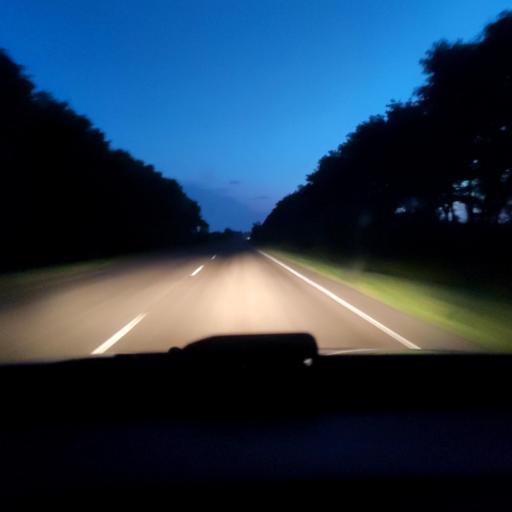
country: RU
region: Voronezj
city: Panino
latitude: 51.6304
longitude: 40.0588
